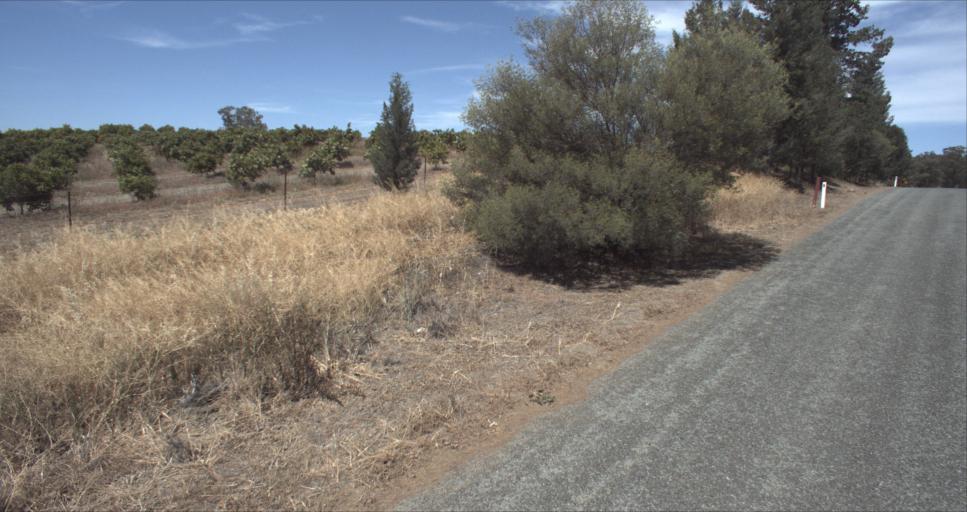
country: AU
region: New South Wales
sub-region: Leeton
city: Leeton
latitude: -34.6672
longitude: 146.4468
